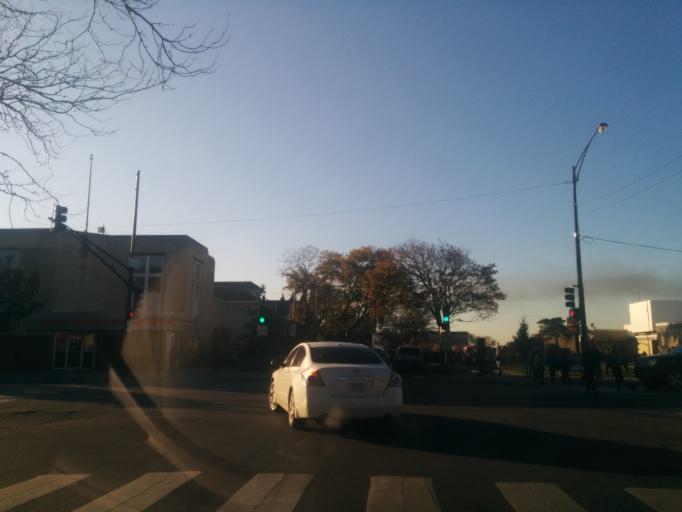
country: US
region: Illinois
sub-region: Cook County
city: Oak Park
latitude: 41.9243
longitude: -87.7611
